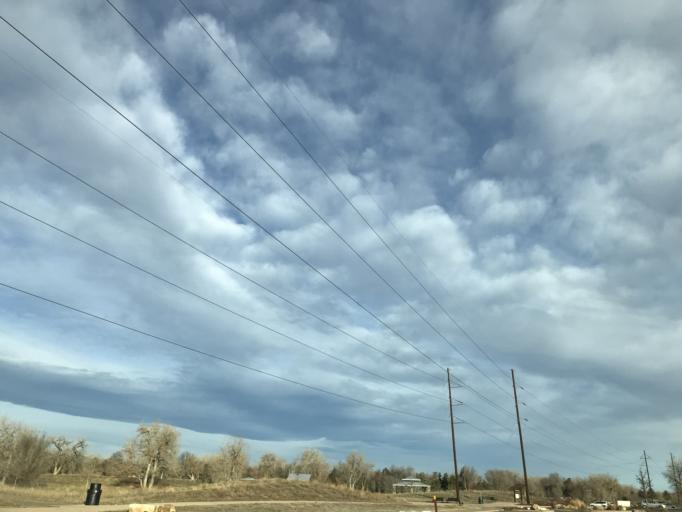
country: US
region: Colorado
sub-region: Arapahoe County
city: Columbine Valley
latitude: 39.5946
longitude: -105.0261
